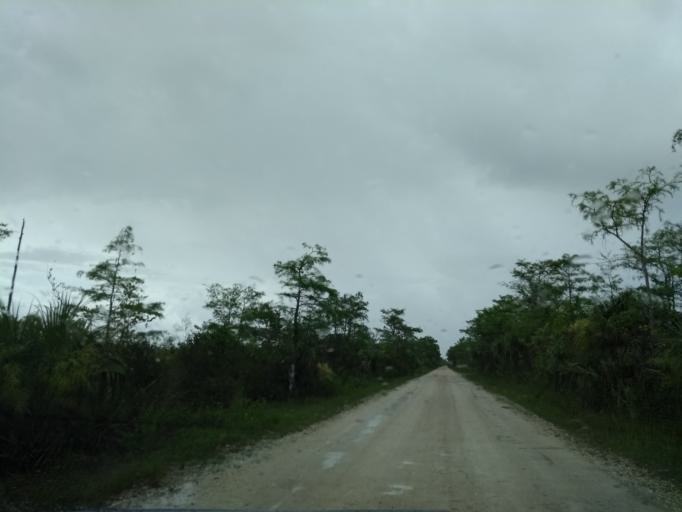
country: US
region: Florida
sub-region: Miami-Dade County
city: The Hammocks
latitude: 25.7603
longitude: -81.0141
